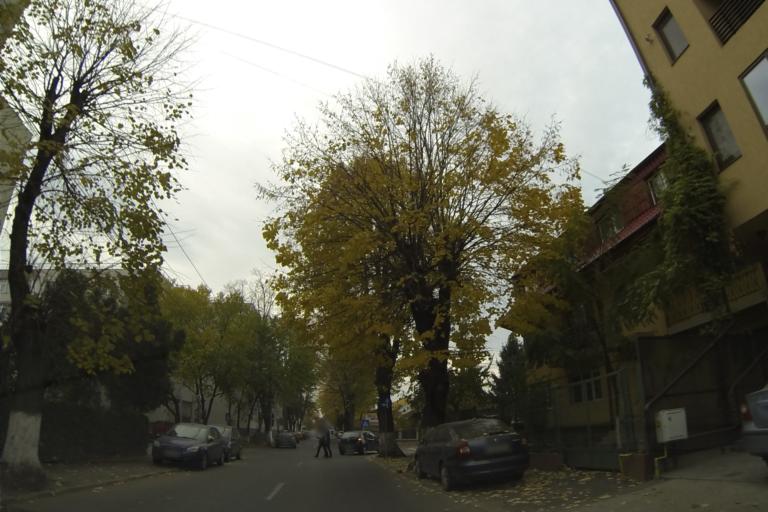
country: RO
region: Ilfov
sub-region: Comuna Chiajna
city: Rosu
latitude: 44.4357
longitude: 26.0109
